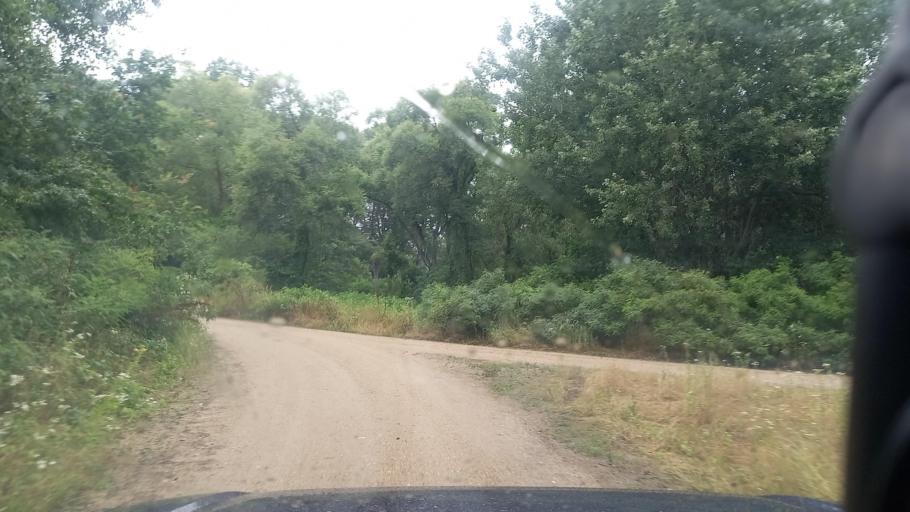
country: RU
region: Krasnodarskiy
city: Vasyurinskaya
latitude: 45.0324
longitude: 39.4748
